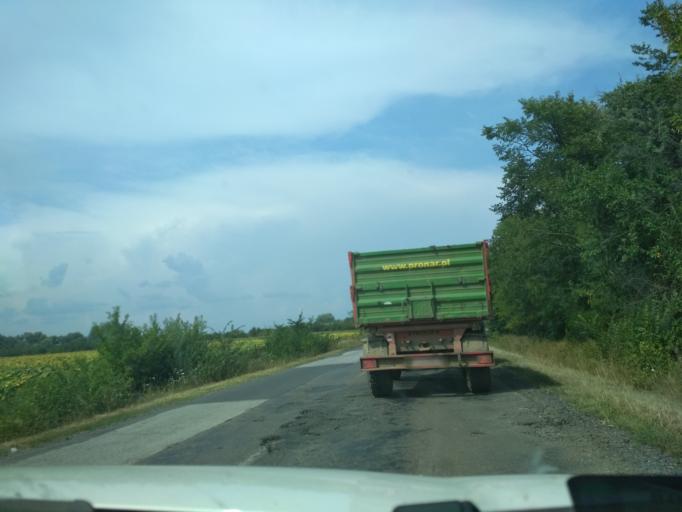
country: HU
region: Jasz-Nagykun-Szolnok
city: Abadszalok
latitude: 47.5014
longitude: 20.6280
